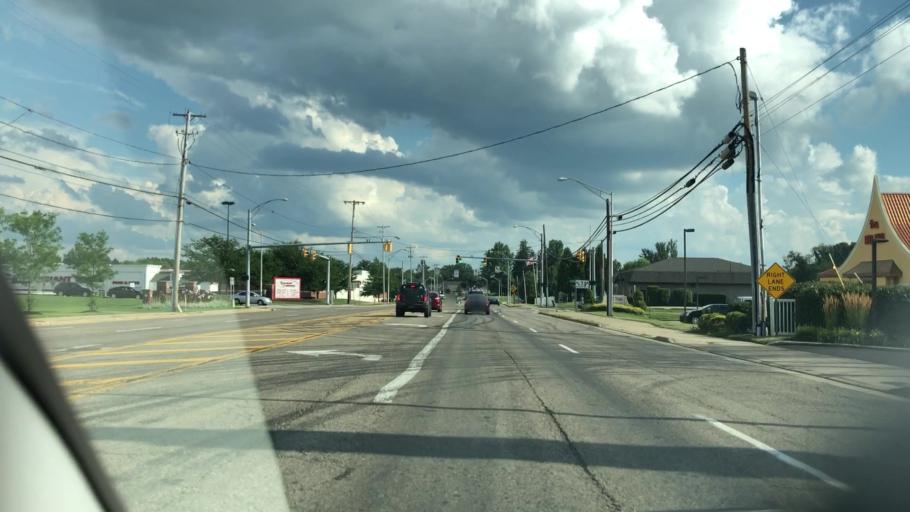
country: US
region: Ohio
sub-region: Summit County
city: Montrose-Ghent
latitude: 41.1348
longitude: -81.6372
